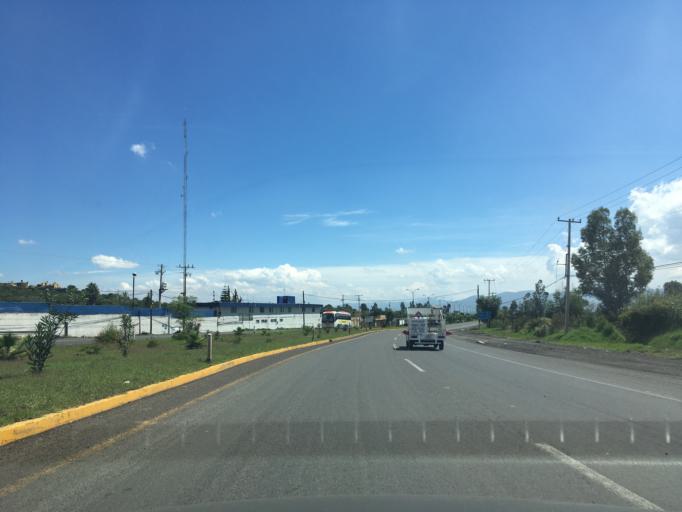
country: MX
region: Michoacan
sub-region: Morelia
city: Lomas de la Maestranza
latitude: 19.6854
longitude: -101.3397
